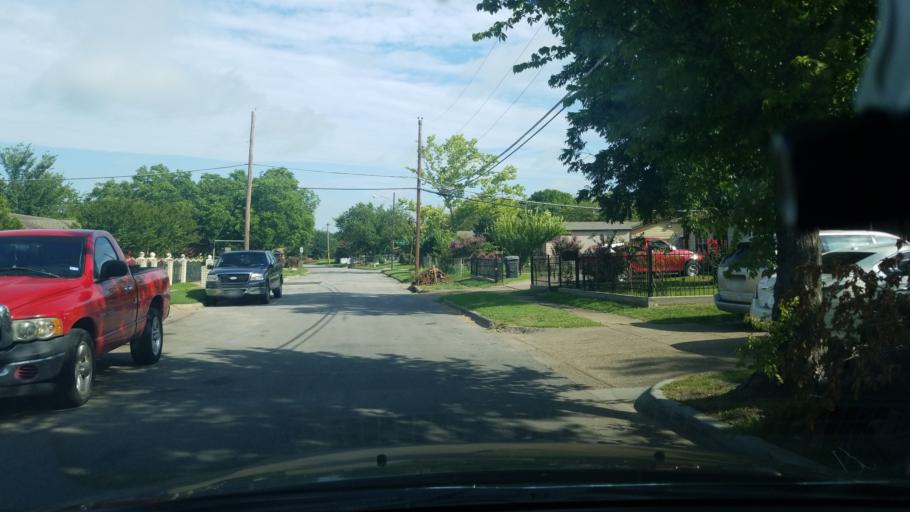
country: US
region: Texas
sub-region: Dallas County
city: Balch Springs
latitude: 32.7470
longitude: -96.6719
